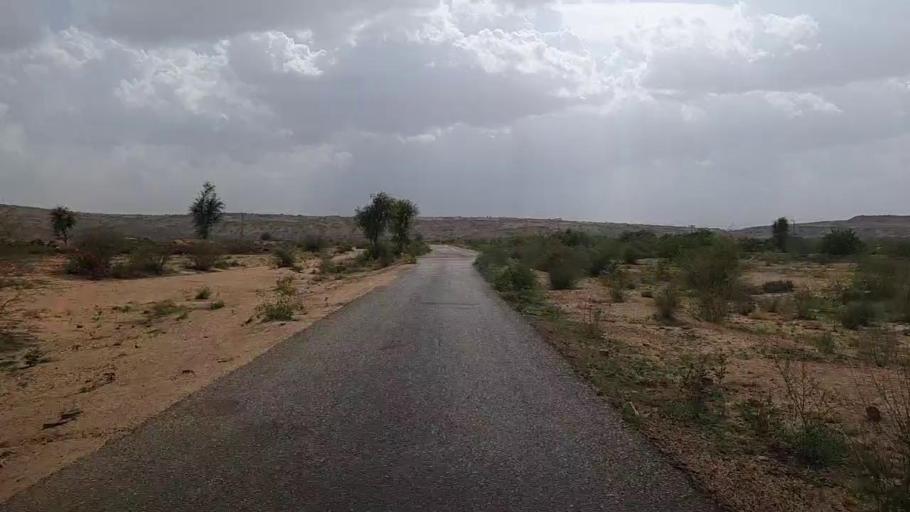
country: PK
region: Sindh
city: Jamshoro
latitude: 25.3949
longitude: 67.7542
